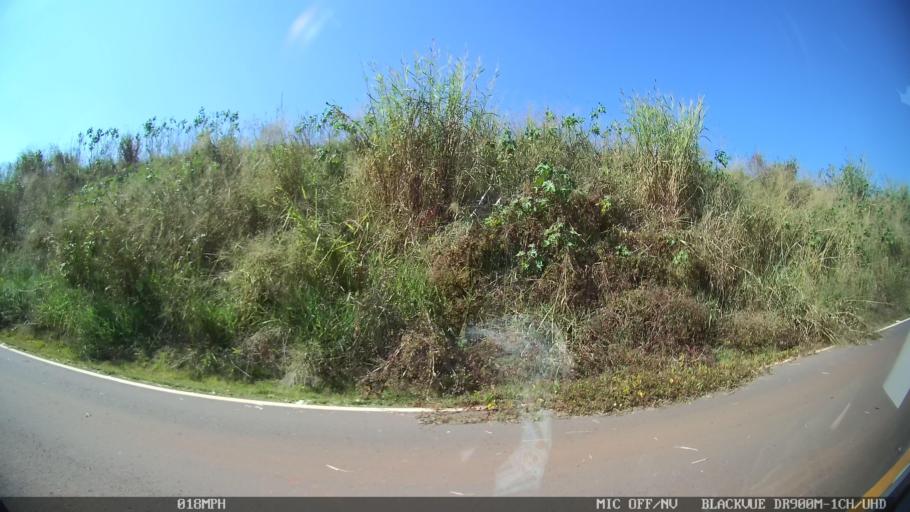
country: BR
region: Sao Paulo
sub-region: Valinhos
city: Valinhos
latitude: -23.0217
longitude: -47.0874
